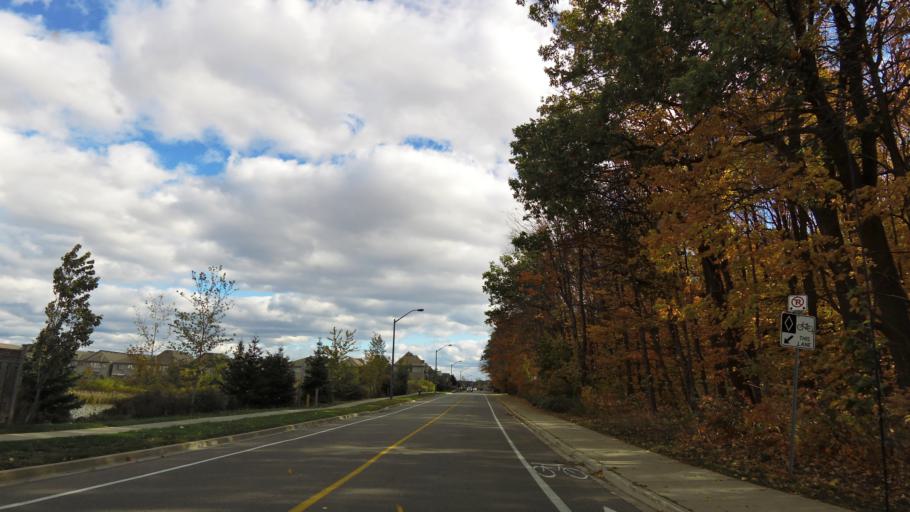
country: CA
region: Ontario
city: Burlington
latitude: 43.4258
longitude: -79.7770
